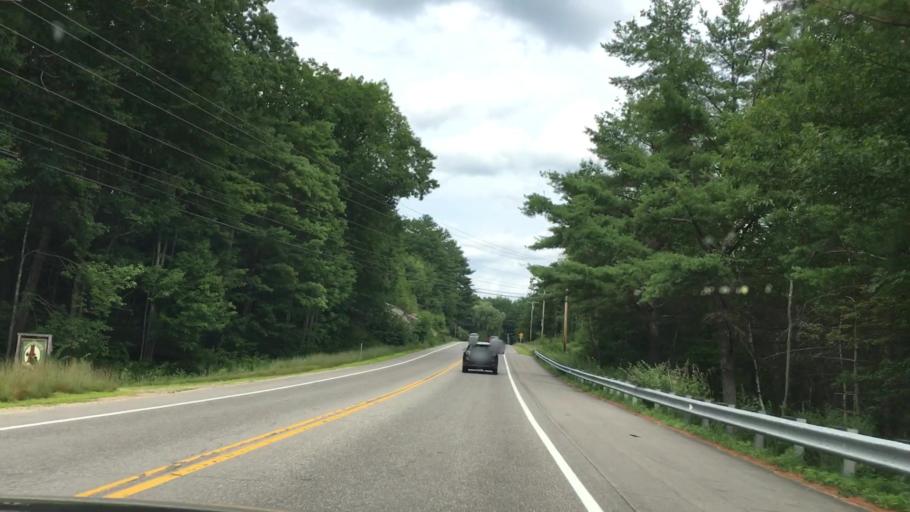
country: US
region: New Hampshire
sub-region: Belknap County
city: Meredith
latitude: 43.6225
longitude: -71.5595
